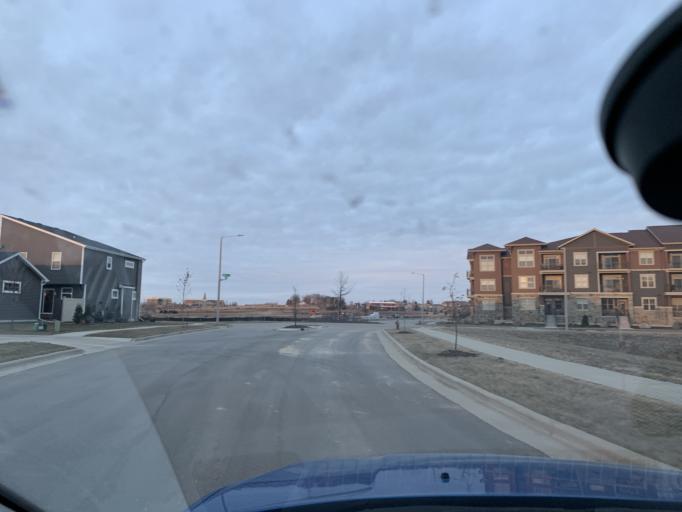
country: US
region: Wisconsin
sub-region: Dane County
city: Verona
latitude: 43.0513
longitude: -89.5553
